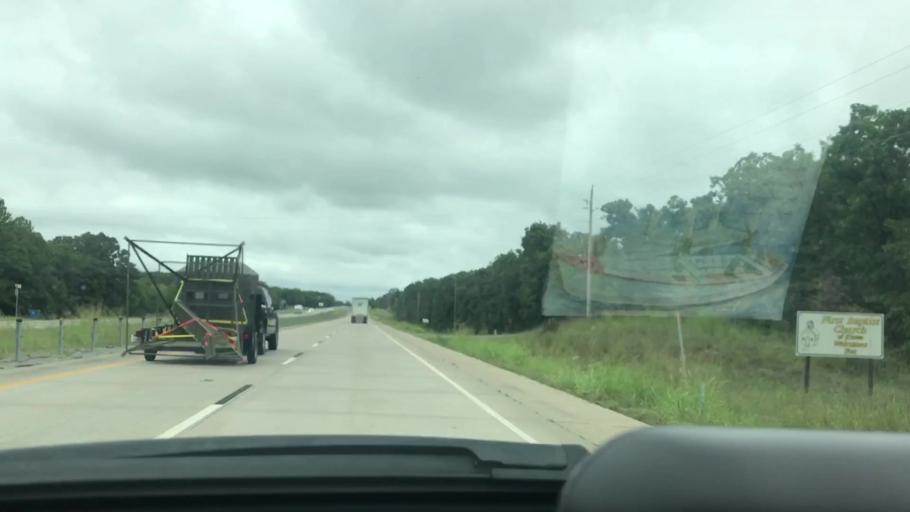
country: US
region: Oklahoma
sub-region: Pittsburg County
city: McAlester
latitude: 34.7036
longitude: -95.9065
